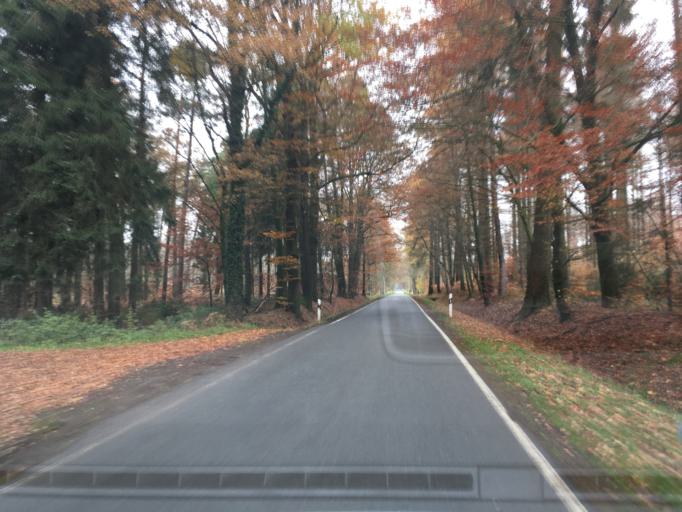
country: DE
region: North Rhine-Westphalia
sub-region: Regierungsbezirk Munster
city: Gescher
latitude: 52.0132
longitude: 6.9968
